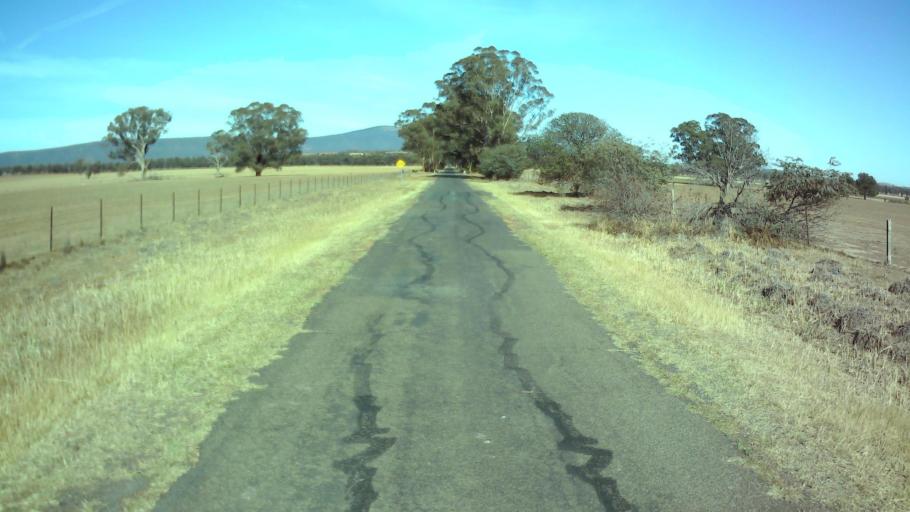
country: AU
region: New South Wales
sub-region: Weddin
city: Grenfell
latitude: -33.9069
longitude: 148.1002
